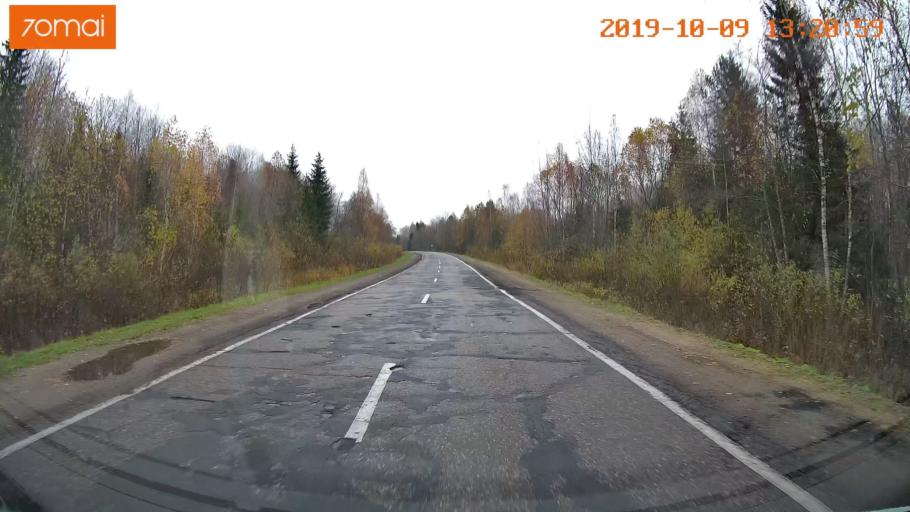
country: RU
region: Jaroslavl
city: Lyubim
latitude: 58.3413
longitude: 40.8386
